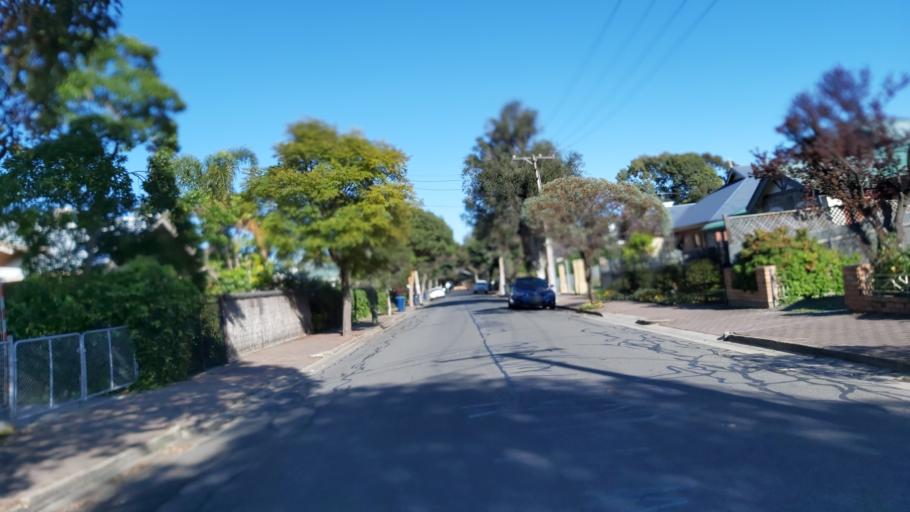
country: AU
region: South Australia
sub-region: Unley
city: Fullarton
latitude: -34.9523
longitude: 138.6183
